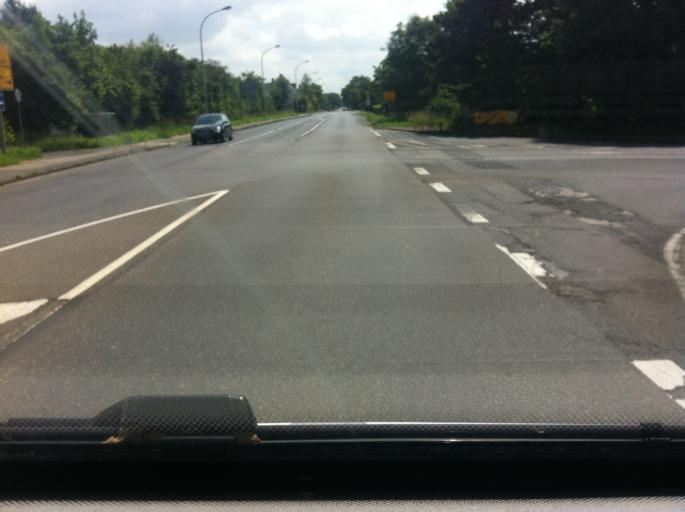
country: DE
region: North Rhine-Westphalia
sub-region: Regierungsbezirk Koln
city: Euskirchen
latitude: 50.7090
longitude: 6.8146
